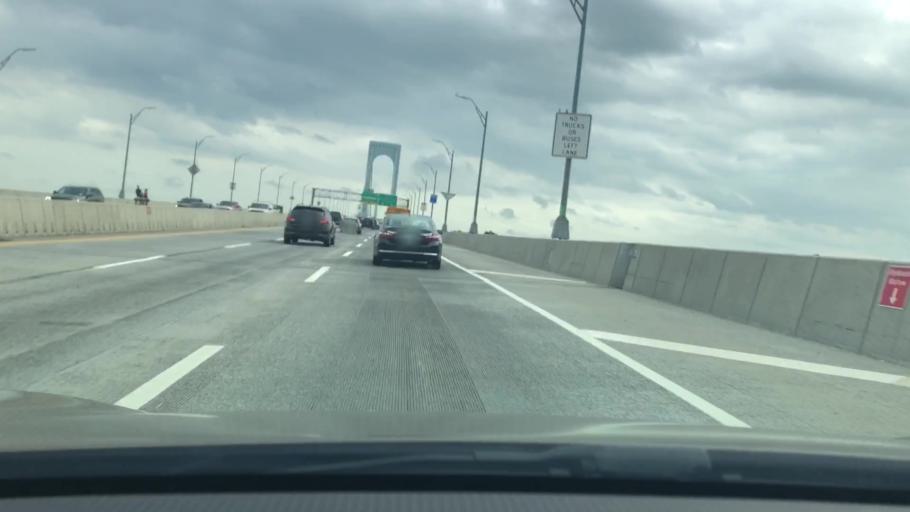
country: US
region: New York
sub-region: Bronx
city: The Bronx
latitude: 40.8113
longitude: -73.8359
